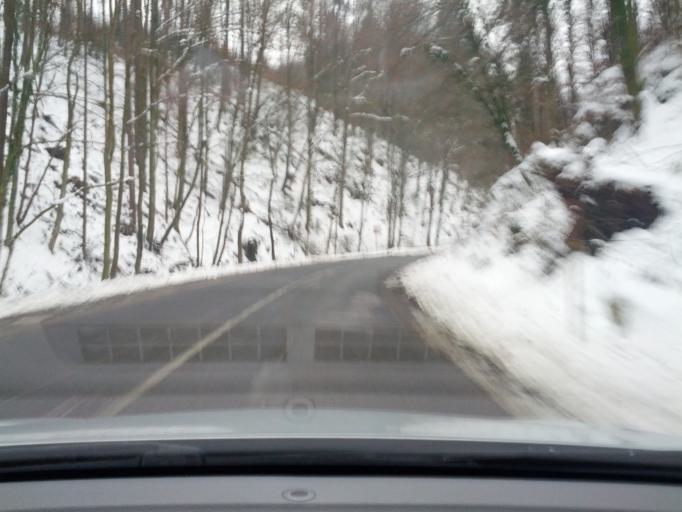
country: SI
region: Moravce
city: Moravce
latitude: 46.1373
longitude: 14.8049
